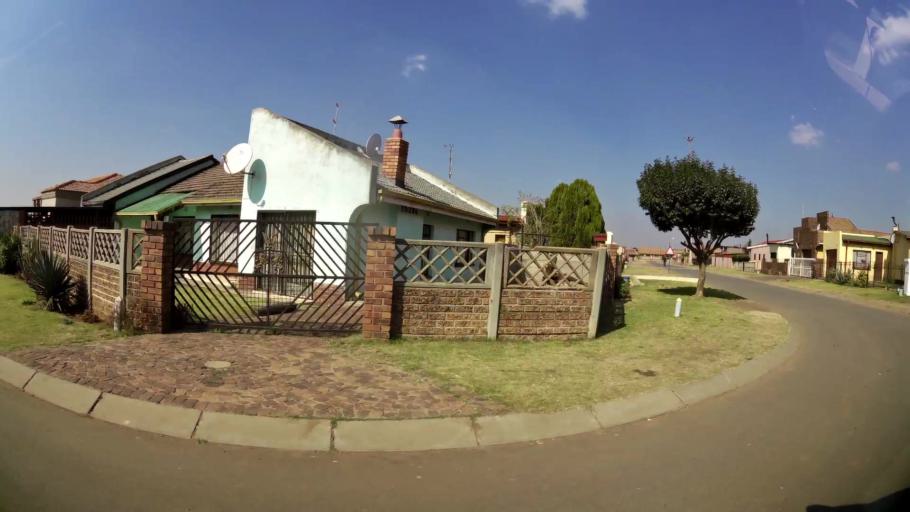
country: ZA
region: Gauteng
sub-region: Ekurhuleni Metropolitan Municipality
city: Benoni
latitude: -26.1395
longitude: 28.4125
